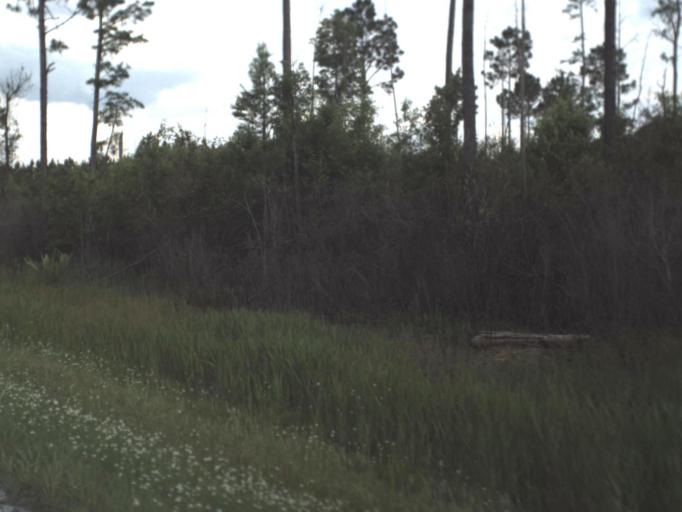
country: US
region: Florida
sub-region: Baker County
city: Macclenny
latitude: 30.5340
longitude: -82.3198
